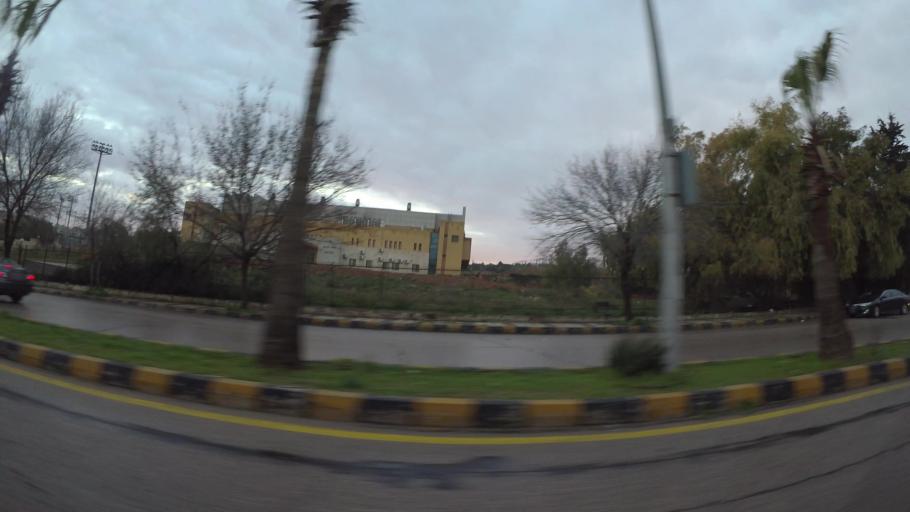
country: JO
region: Amman
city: Amman
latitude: 31.9828
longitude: 35.9107
